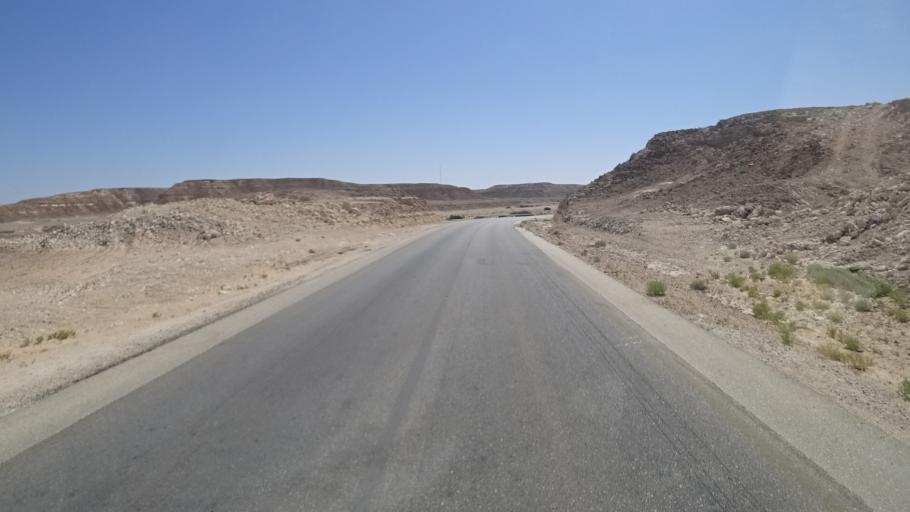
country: OM
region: Zufar
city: Salalah
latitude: 17.4972
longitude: 53.3624
